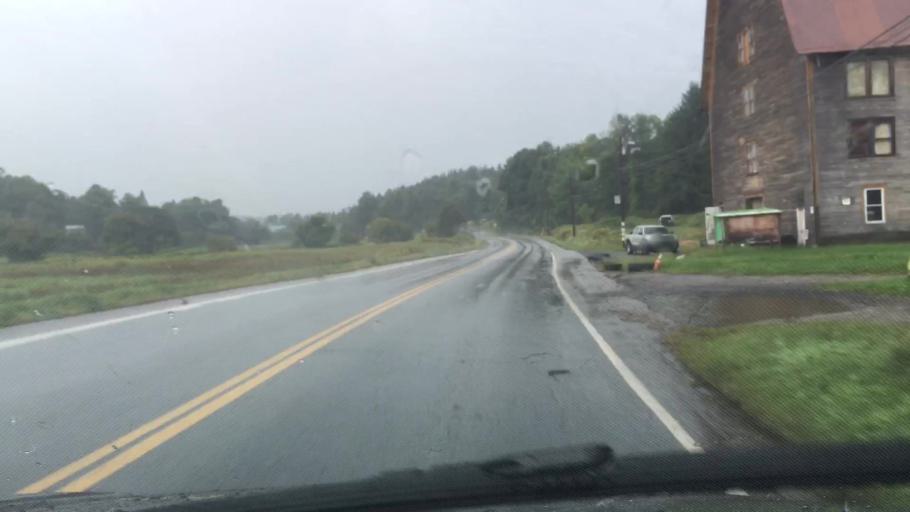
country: US
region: Vermont
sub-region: Washington County
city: Barre
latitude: 44.2869
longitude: -72.4092
